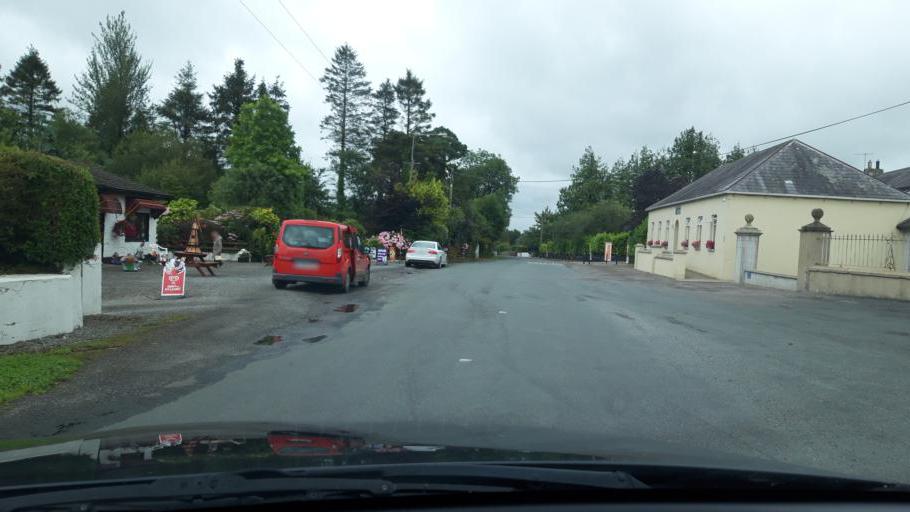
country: IE
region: Munster
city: Cahir
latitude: 52.1835
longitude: -7.8480
